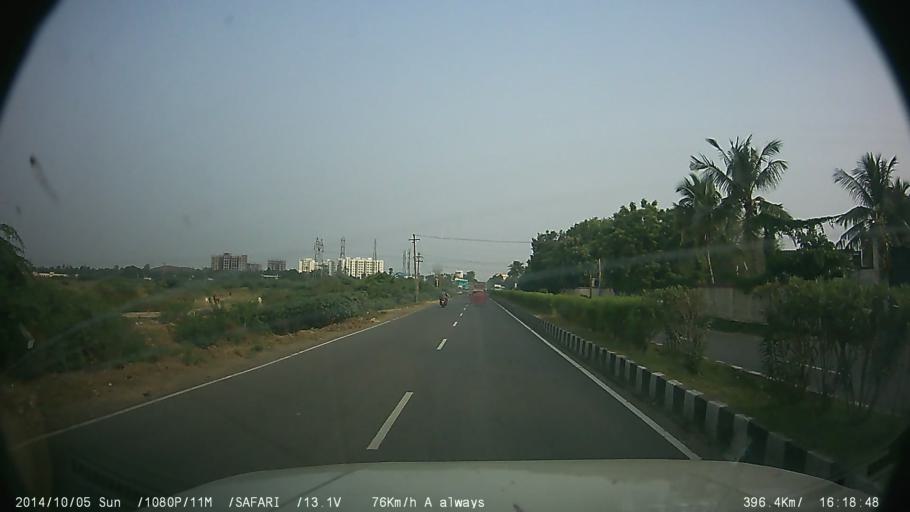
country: IN
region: Tamil Nadu
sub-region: Kancheepuram
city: Vengavasal
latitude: 12.8559
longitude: 80.1358
